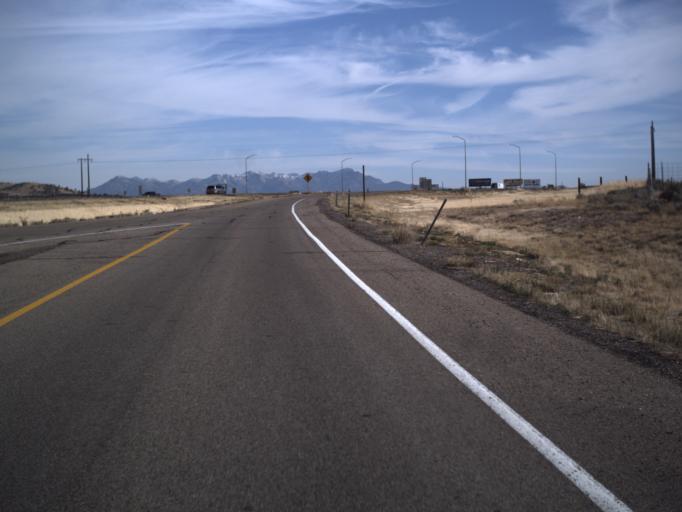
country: US
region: Utah
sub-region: Millard County
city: Fillmore
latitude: 38.9917
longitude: -112.3223
